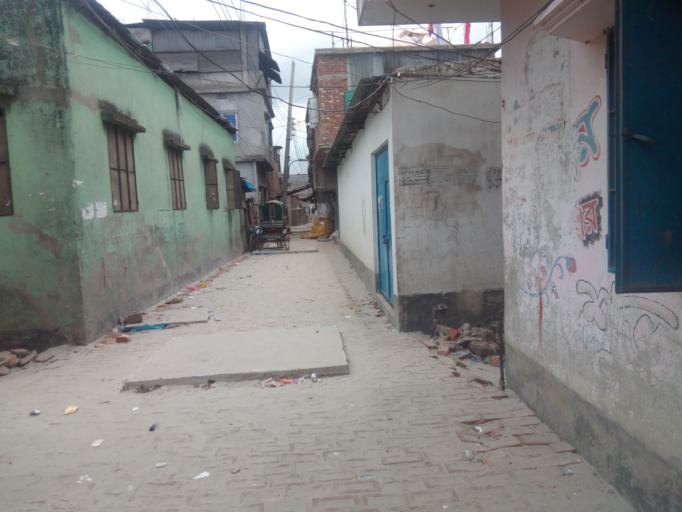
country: BD
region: Dhaka
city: Azimpur
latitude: 23.7087
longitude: 90.3776
